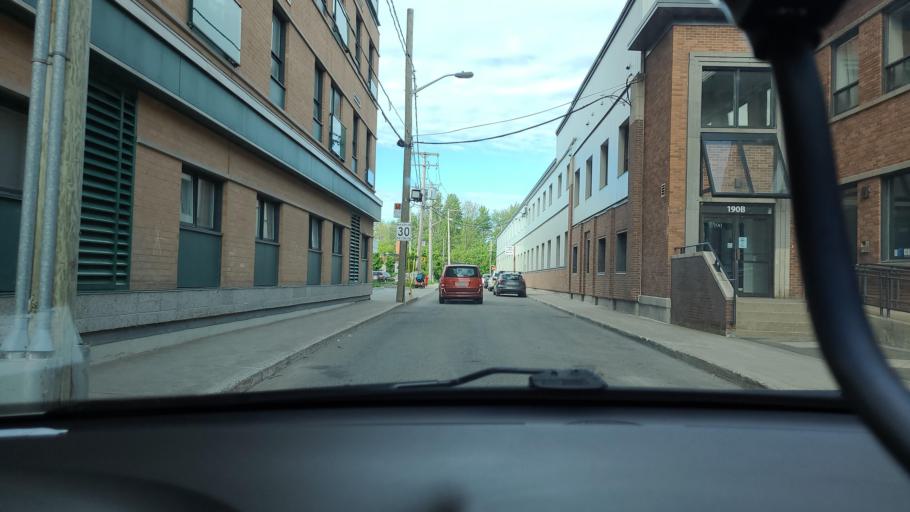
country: CA
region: Quebec
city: Quebec
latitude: 46.8159
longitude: -71.2294
